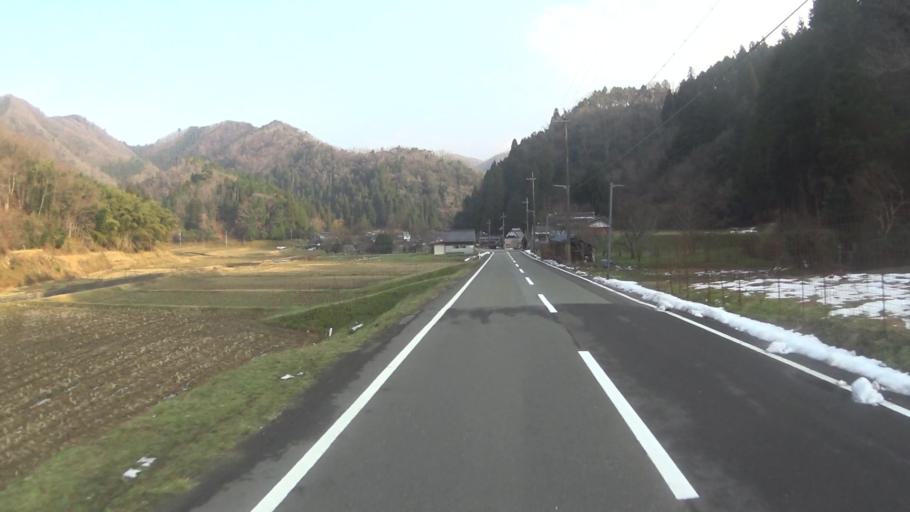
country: JP
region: Kyoto
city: Maizuru
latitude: 35.4095
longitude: 135.4133
